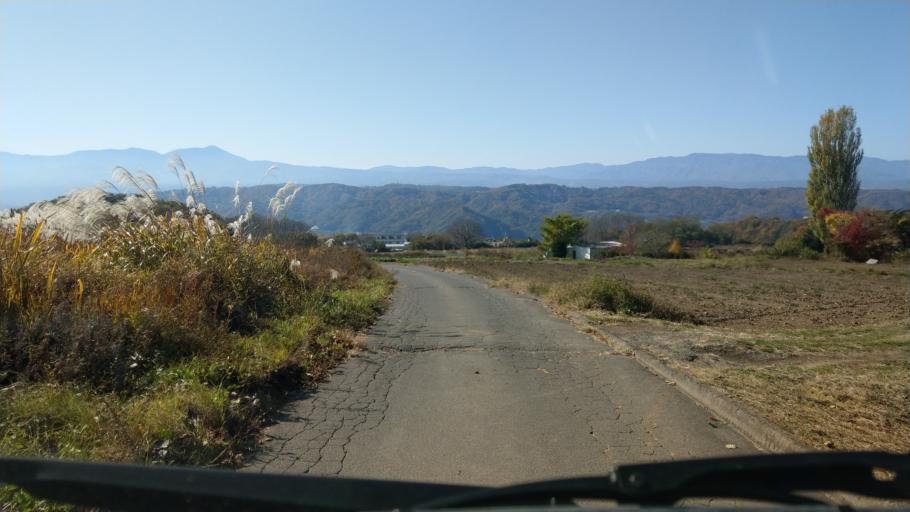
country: JP
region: Nagano
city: Komoro
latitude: 36.3438
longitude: 138.4334
